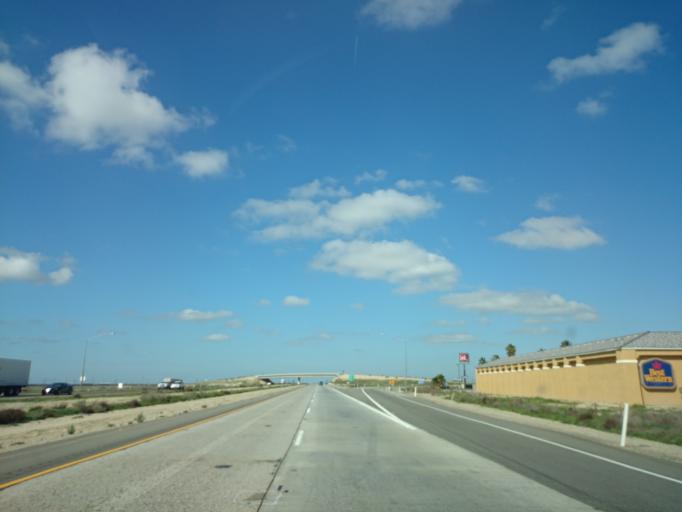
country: US
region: California
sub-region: Kern County
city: Buttonwillow
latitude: 35.3523
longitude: -119.3319
